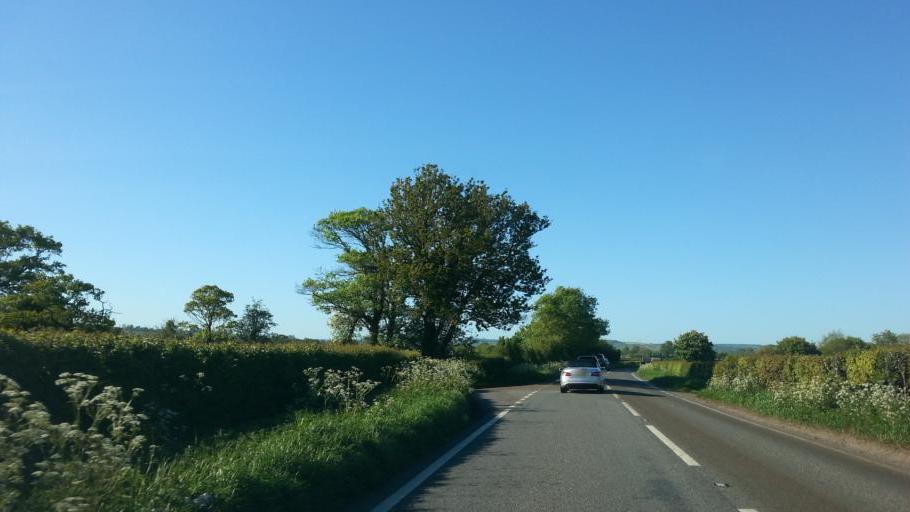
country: GB
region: England
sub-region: Somerset
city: Castle Cary
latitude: 51.1107
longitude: -2.5201
